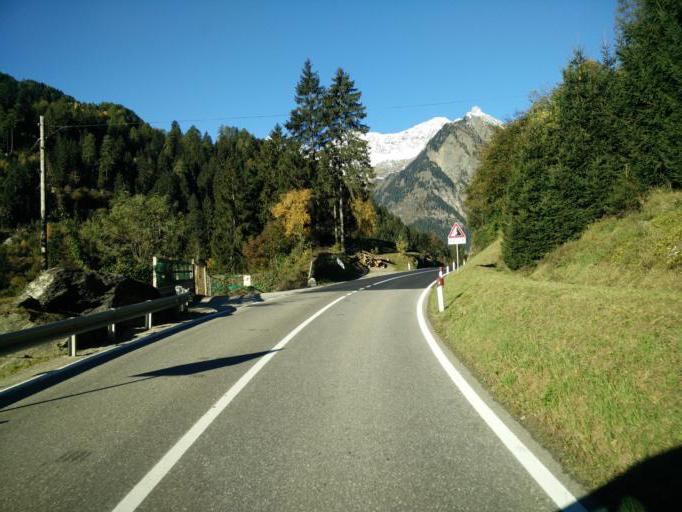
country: IT
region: Trentino-Alto Adige
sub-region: Bolzano
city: Moso in Passiria
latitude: 46.8225
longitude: 11.1968
